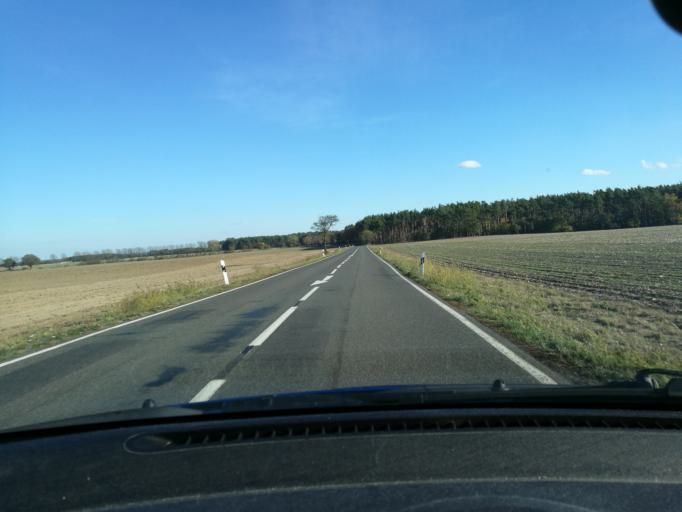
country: DE
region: Brandenburg
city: Karstadt
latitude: 53.1652
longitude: 11.6459
